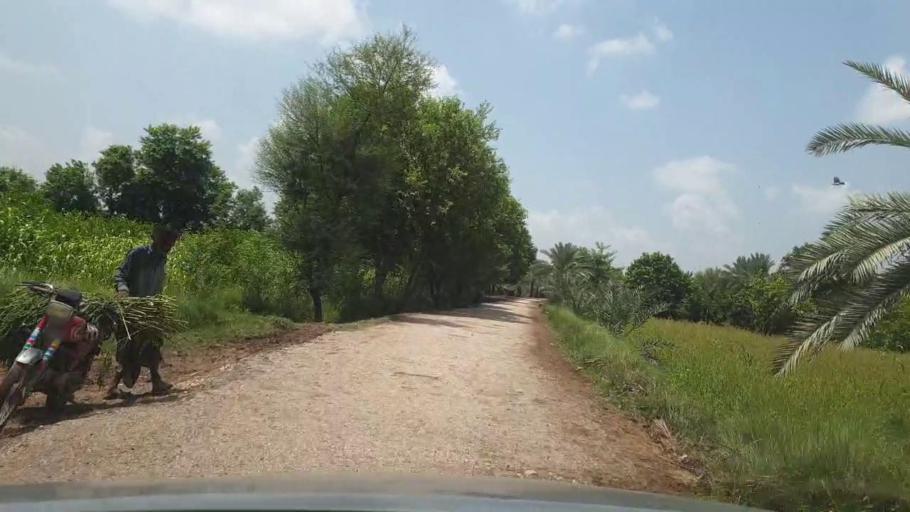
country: PK
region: Sindh
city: Pir jo Goth
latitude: 27.6099
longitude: 68.6092
